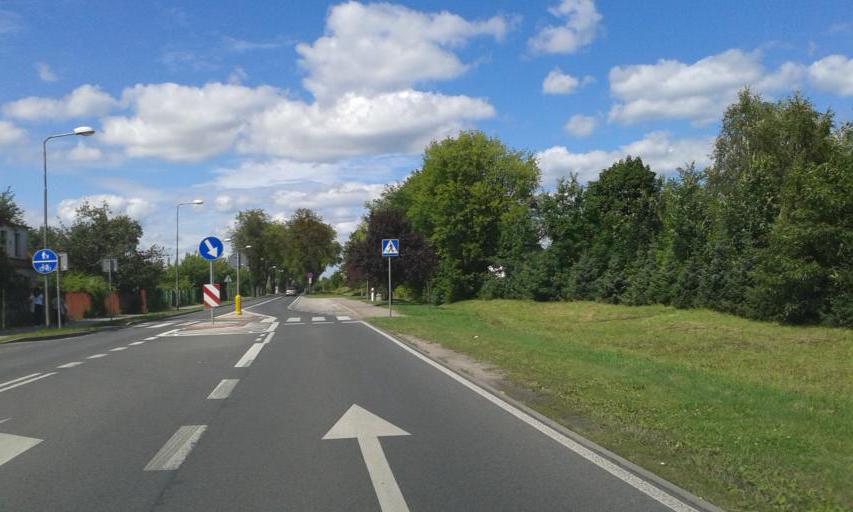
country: PL
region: West Pomeranian Voivodeship
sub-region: Powiat walecki
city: Walcz
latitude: 53.2826
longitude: 16.4625
